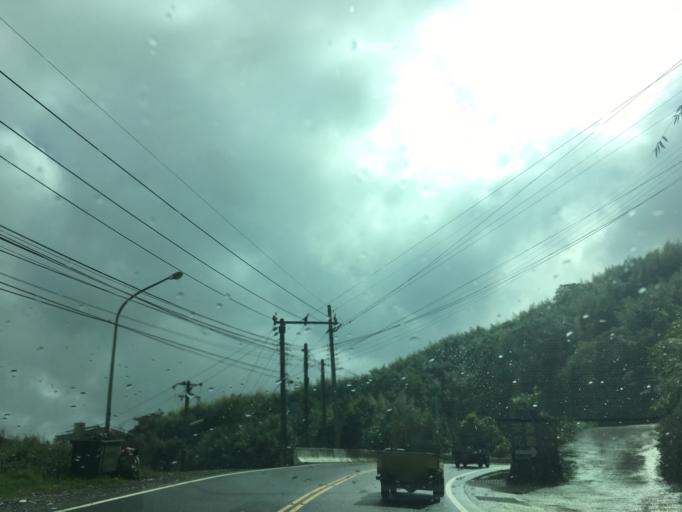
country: TW
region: Taiwan
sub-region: Chiayi
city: Jiayi Shi
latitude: 23.4462
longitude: 120.6754
